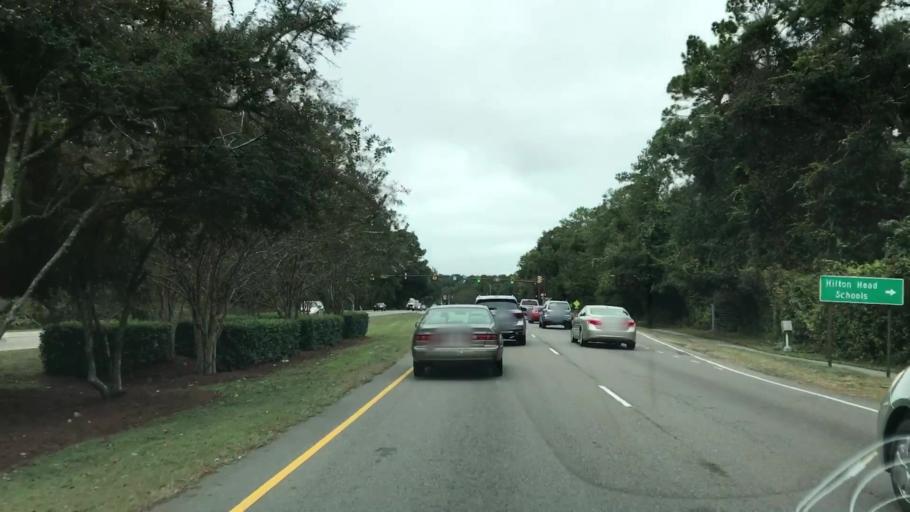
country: US
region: South Carolina
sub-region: Beaufort County
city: Hilton Head Island
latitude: 32.2141
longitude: -80.7316
